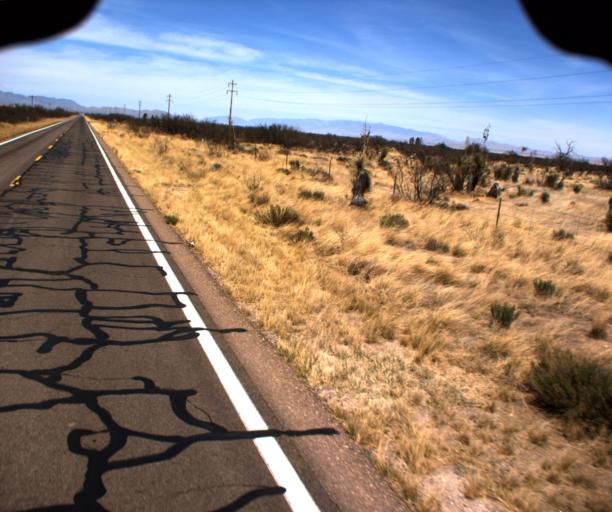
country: US
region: Arizona
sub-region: Cochise County
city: Willcox
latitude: 32.0662
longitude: -109.8942
